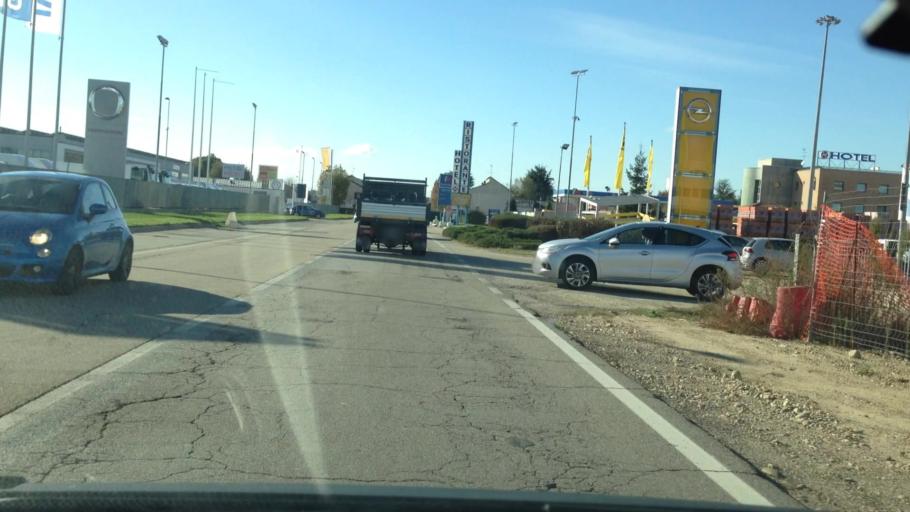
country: IT
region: Piedmont
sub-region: Provincia di Asti
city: Azzano d'Asti
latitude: 44.9067
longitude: 8.2633
